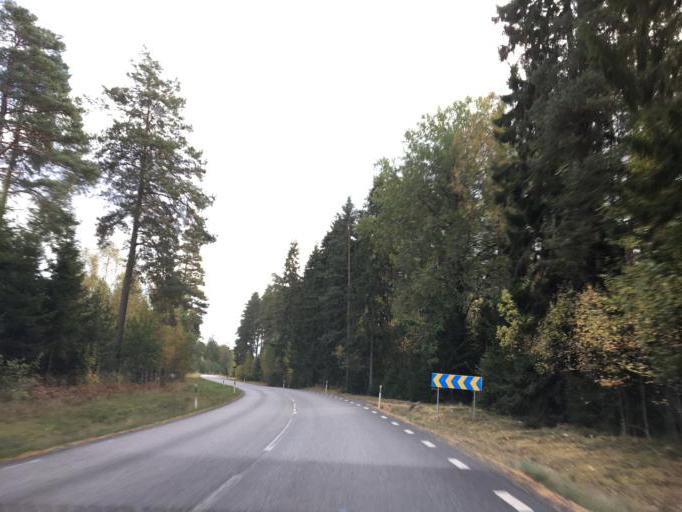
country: SE
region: Soedermanland
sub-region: Flens Kommun
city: Flen
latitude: 58.9241
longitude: 16.4150
